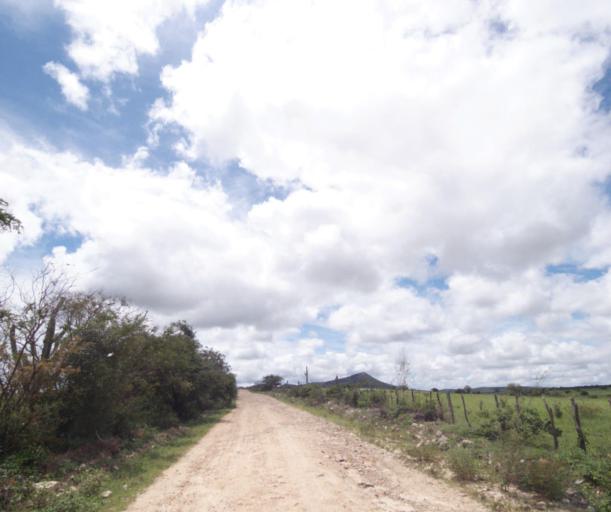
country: BR
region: Bahia
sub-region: Tanhacu
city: Tanhacu
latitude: -14.1752
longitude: -41.1306
